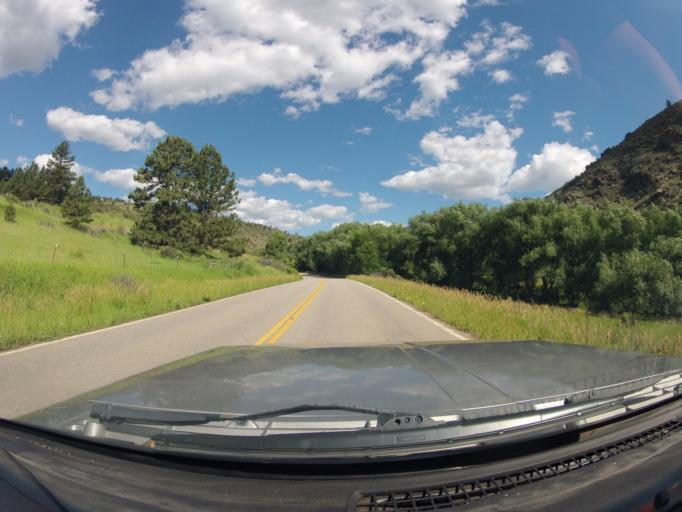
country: US
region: Colorado
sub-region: Larimer County
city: Laporte
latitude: 40.5409
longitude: -105.2801
